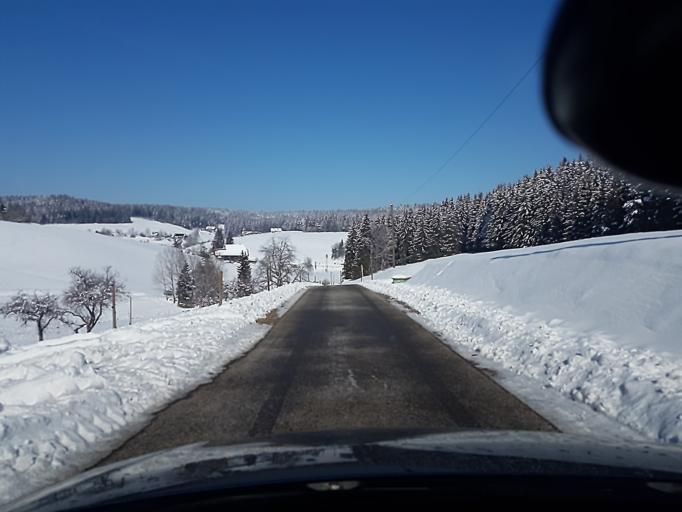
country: DE
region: Baden-Wuerttemberg
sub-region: Freiburg Region
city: Unterkirnach
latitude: 48.1011
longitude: 8.3740
